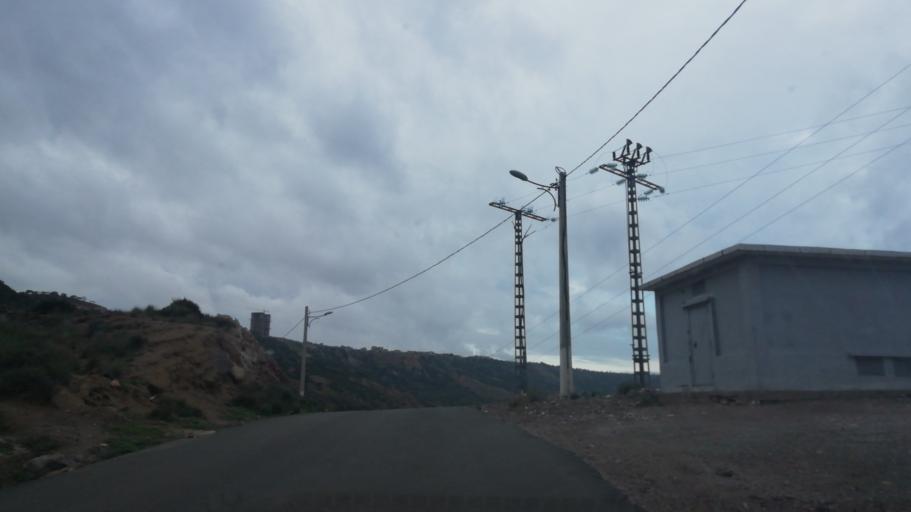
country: DZ
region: Oran
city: Bir el Djir
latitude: 35.7692
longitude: -0.5234
